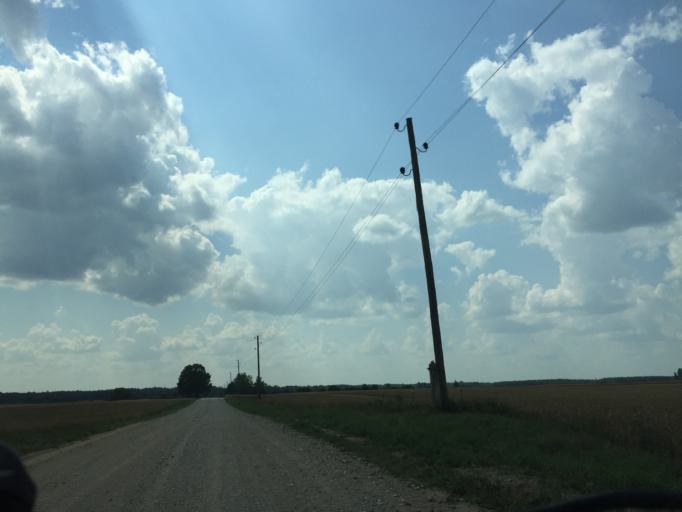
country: LT
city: Zagare
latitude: 56.3852
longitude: 23.1840
